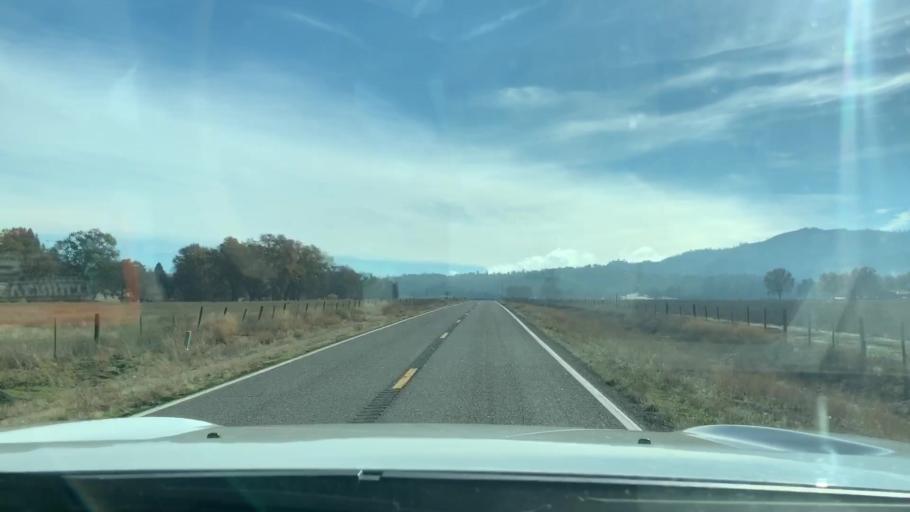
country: US
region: California
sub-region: Fresno County
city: Coalinga
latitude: 36.1798
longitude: -120.6943
